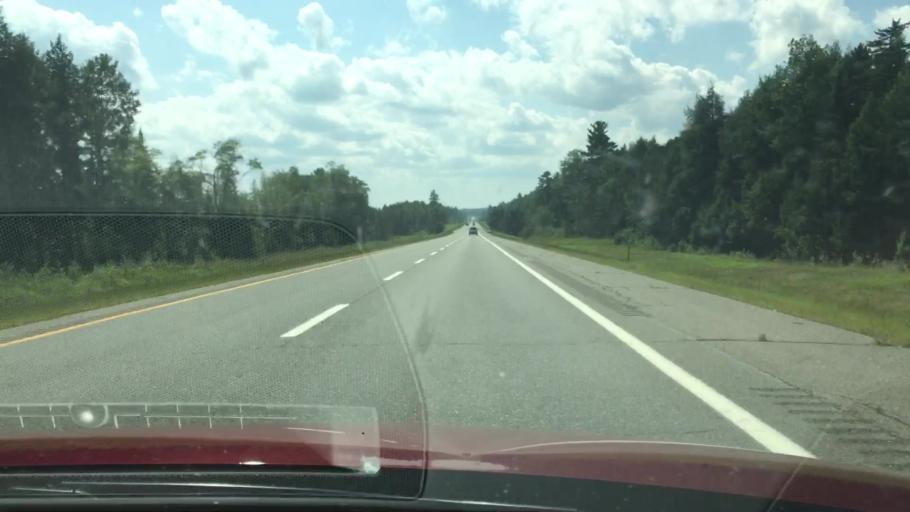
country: US
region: Maine
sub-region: Penobscot County
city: Enfield
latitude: 45.3402
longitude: -68.6243
